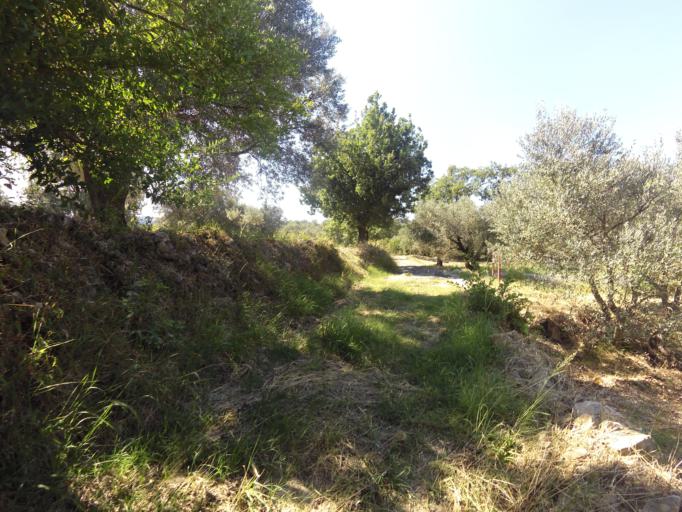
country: IT
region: Calabria
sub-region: Provincia di Reggio Calabria
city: Stilo
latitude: 38.4578
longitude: 16.4598
